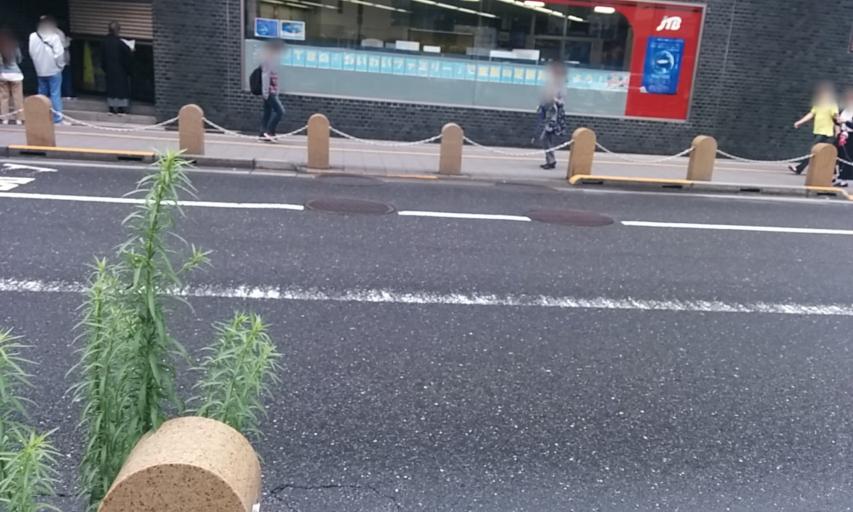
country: JP
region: Tokyo
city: Hachioji
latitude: 35.6567
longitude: 139.3405
